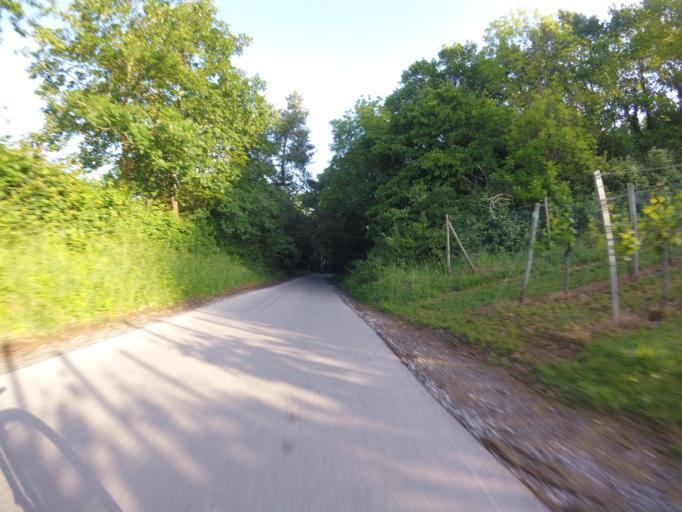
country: DE
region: Baden-Wuerttemberg
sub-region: Regierungsbezirk Stuttgart
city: Abstatt
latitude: 49.0689
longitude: 9.3180
